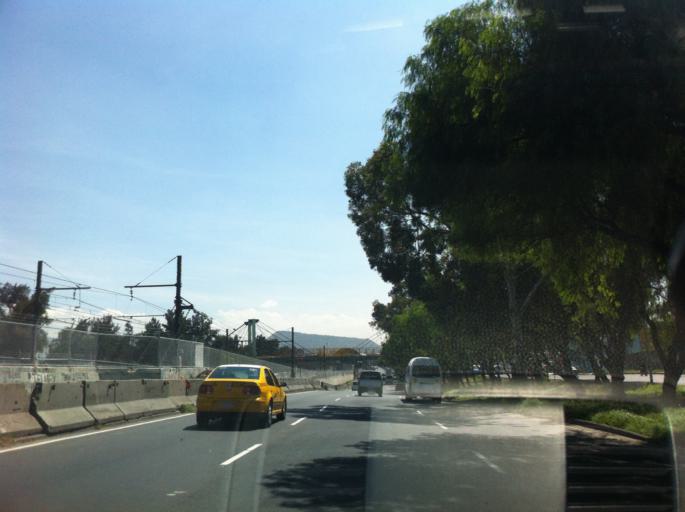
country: MX
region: Mexico
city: Los Reyes La Paz
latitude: 19.3674
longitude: -99.0092
